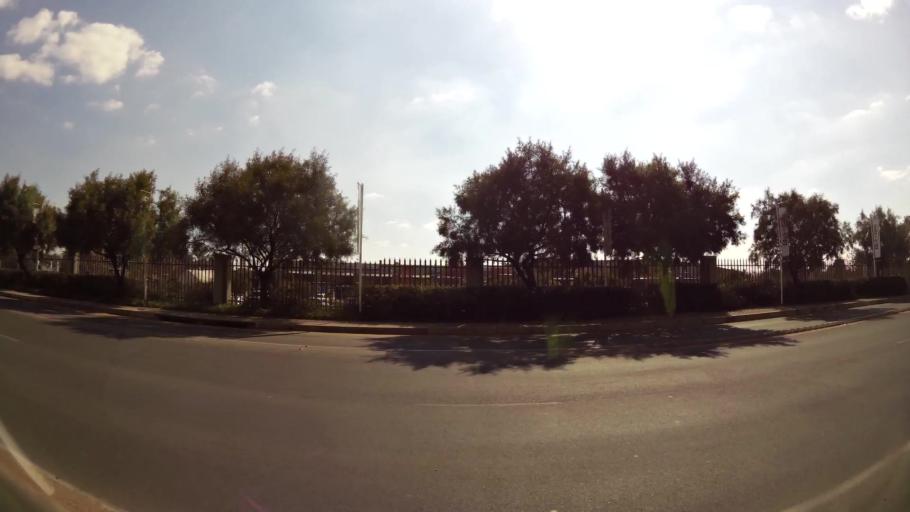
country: ZA
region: Gauteng
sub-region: City of Johannesburg Metropolitan Municipality
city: Modderfontein
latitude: -26.0866
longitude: 28.2526
